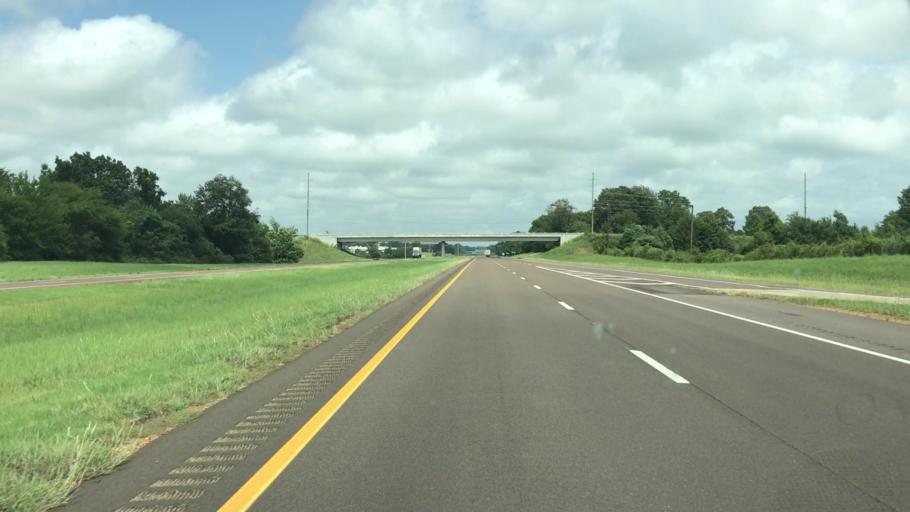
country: US
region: Tennessee
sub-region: Dyer County
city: Dyersburg
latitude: 36.0743
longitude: -89.3457
